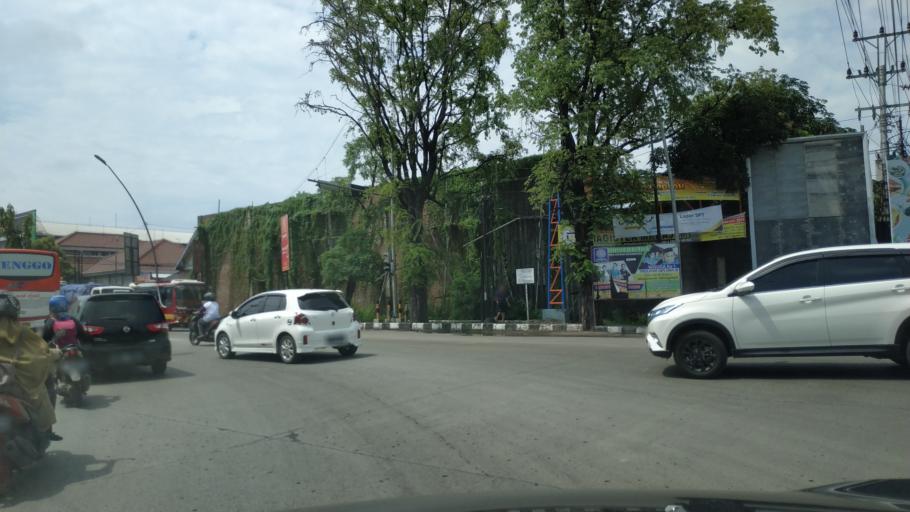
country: ID
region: Central Java
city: Tegal
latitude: -6.8697
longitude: 109.1329
